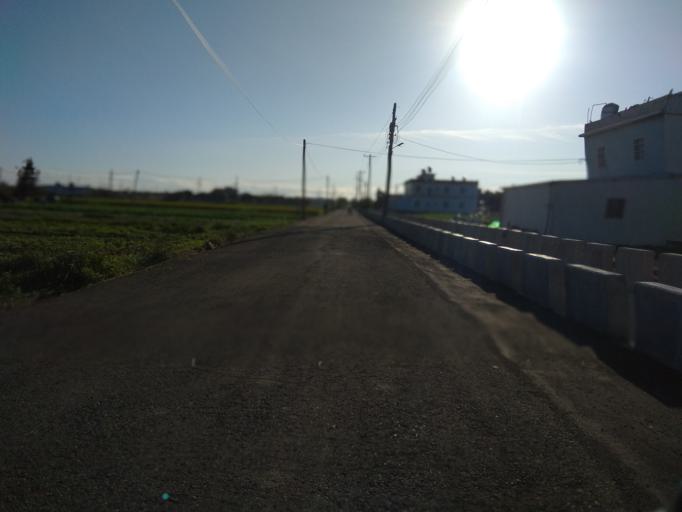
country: TW
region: Taiwan
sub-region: Hsinchu
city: Zhubei
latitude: 24.9878
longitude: 121.0489
